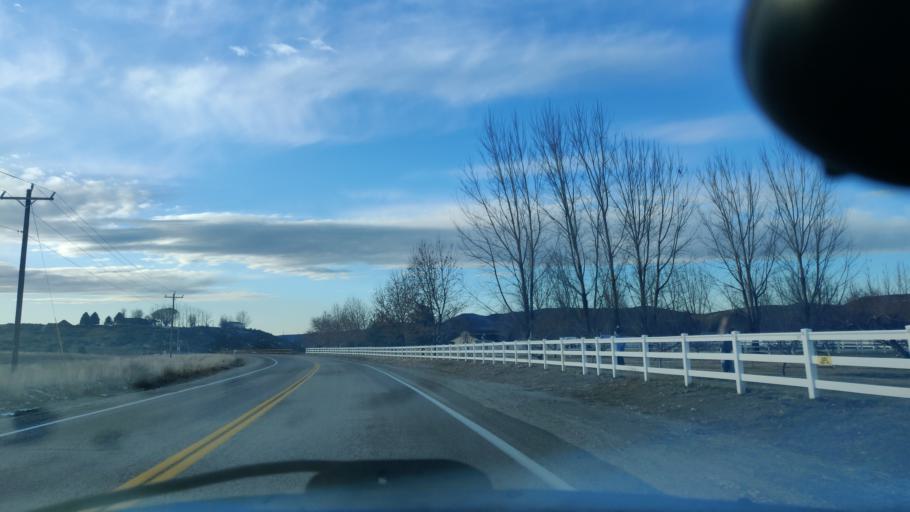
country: US
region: Idaho
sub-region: Ada County
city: Eagle
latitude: 43.7297
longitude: -116.2643
